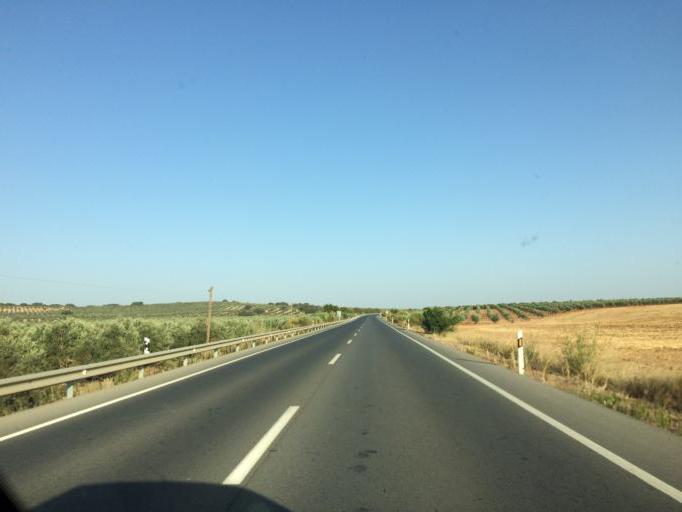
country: ES
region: Andalusia
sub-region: Provincia de Malaga
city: Mollina
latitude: 37.0528
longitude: -4.6621
